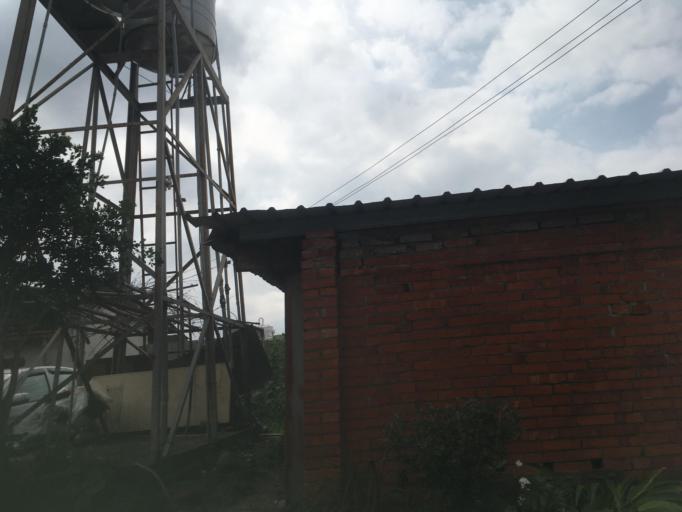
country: TW
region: Taiwan
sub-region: Miaoli
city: Miaoli
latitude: 24.4413
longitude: 120.7084
